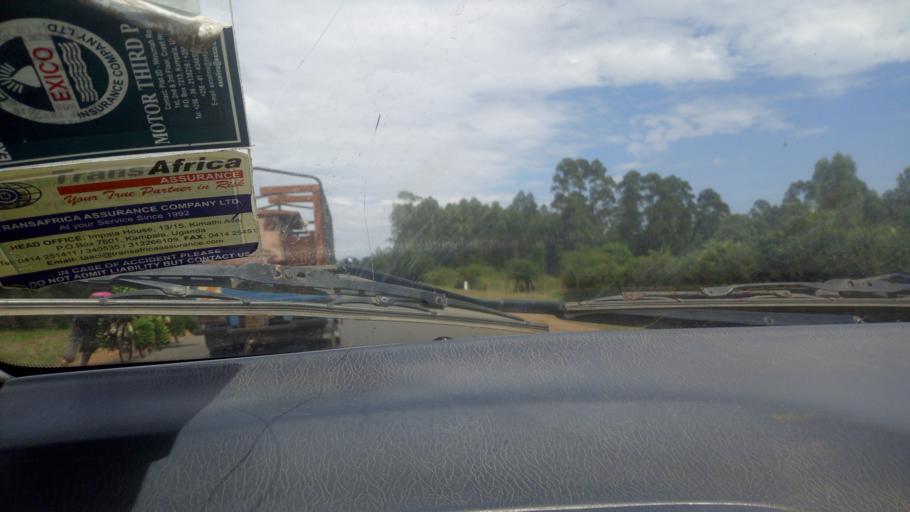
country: UG
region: Western Region
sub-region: Mbarara District
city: Bwizibwera
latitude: -0.4248
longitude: 30.5708
